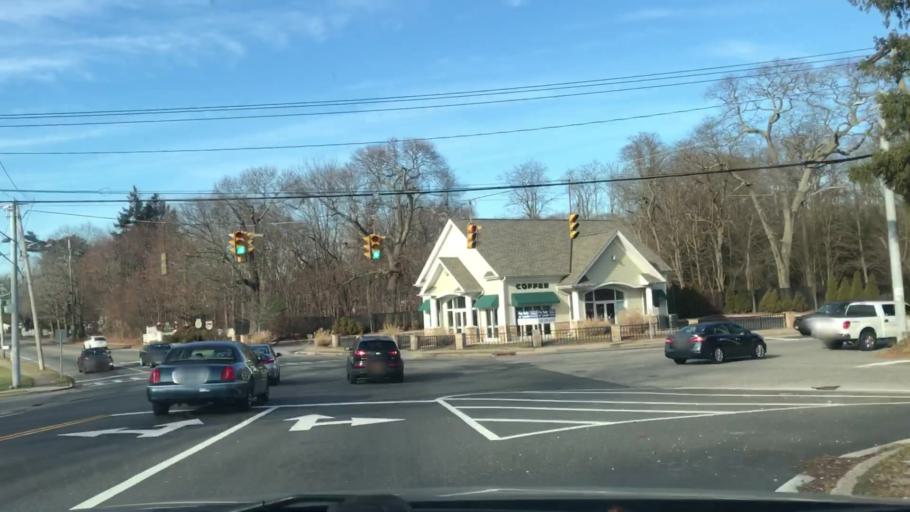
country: US
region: New York
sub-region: Suffolk County
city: Lake Grove
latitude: 40.8371
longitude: -73.1102
